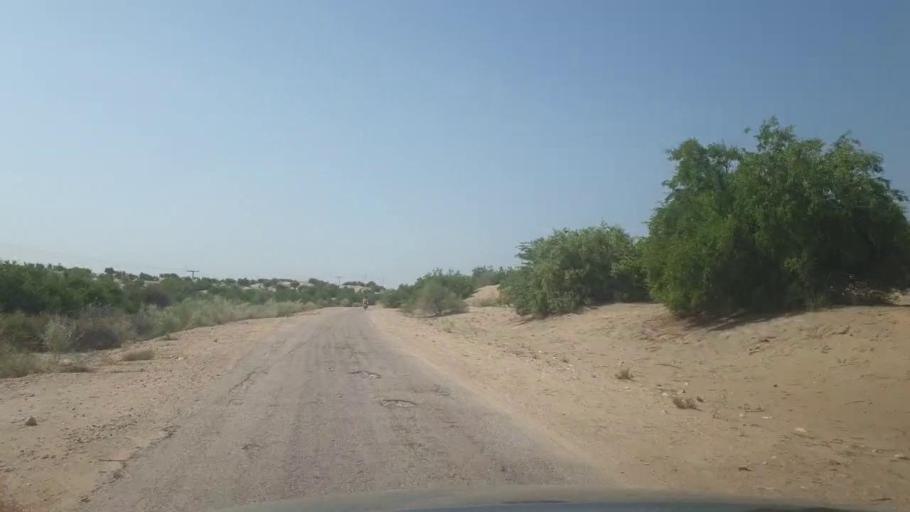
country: PK
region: Sindh
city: Rohri
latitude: 27.4284
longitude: 69.0784
